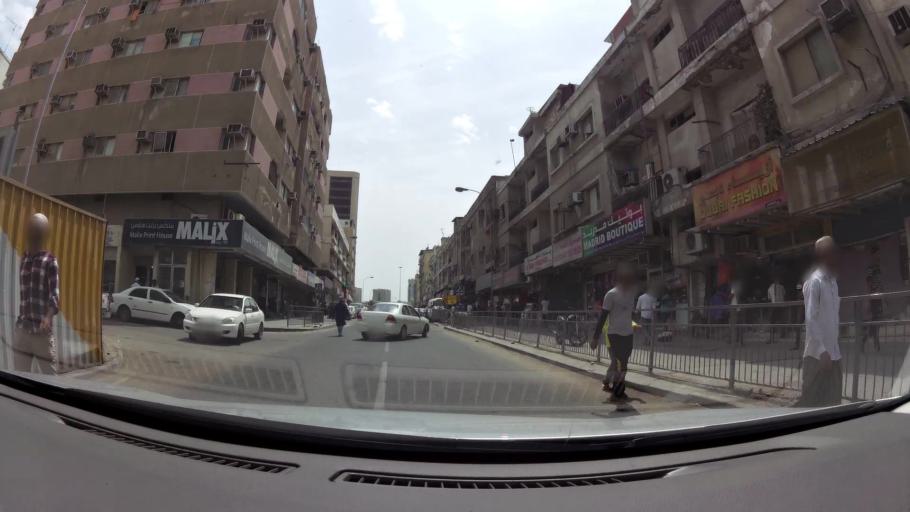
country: QA
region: Baladiyat ad Dawhah
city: Doha
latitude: 25.2821
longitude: 51.5286
